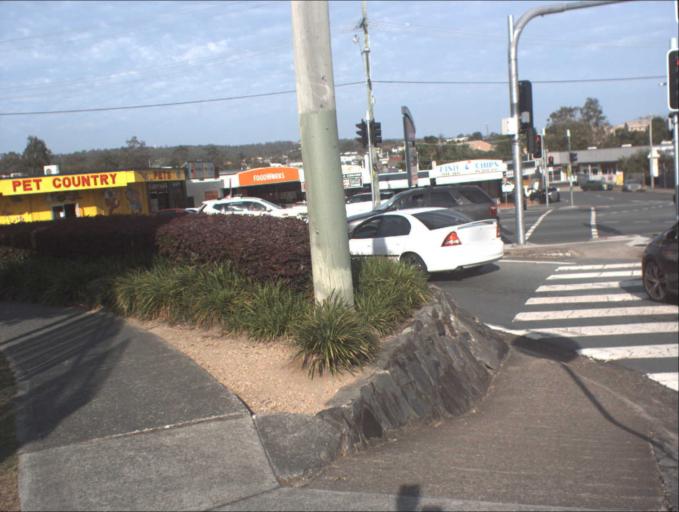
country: AU
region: Queensland
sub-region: Logan
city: Logan City
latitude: -27.6302
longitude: 153.1183
